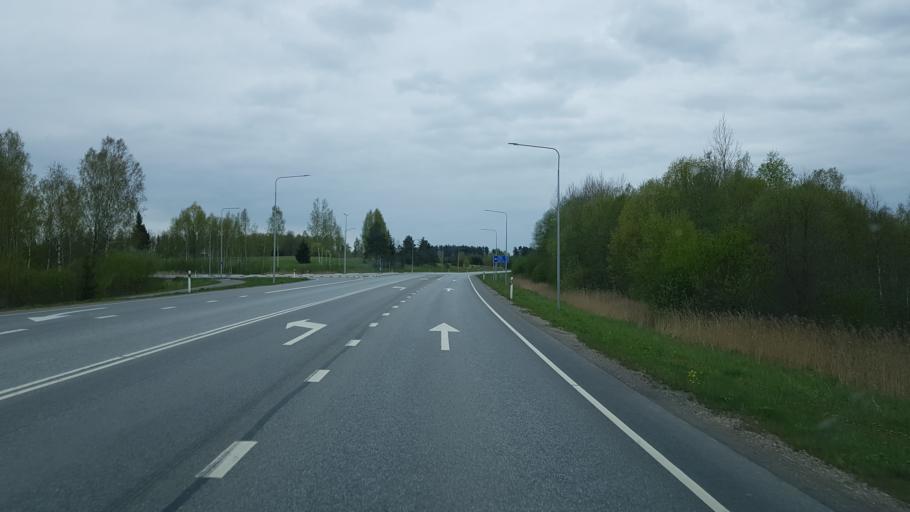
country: EE
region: Viljandimaa
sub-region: Viljandi linn
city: Viljandi
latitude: 58.3300
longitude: 25.5758
